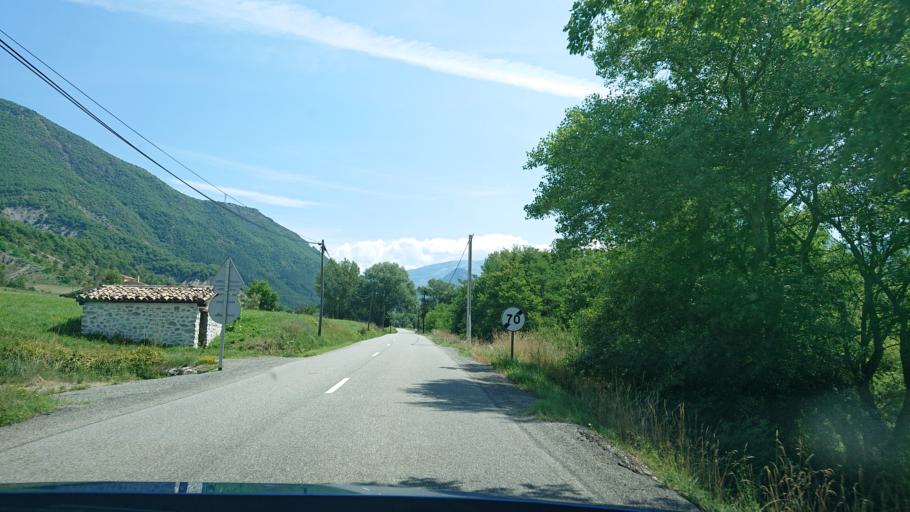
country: FR
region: Provence-Alpes-Cote d'Azur
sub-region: Departement des Alpes-de-Haute-Provence
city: Sisteron
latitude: 44.2609
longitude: 5.9723
